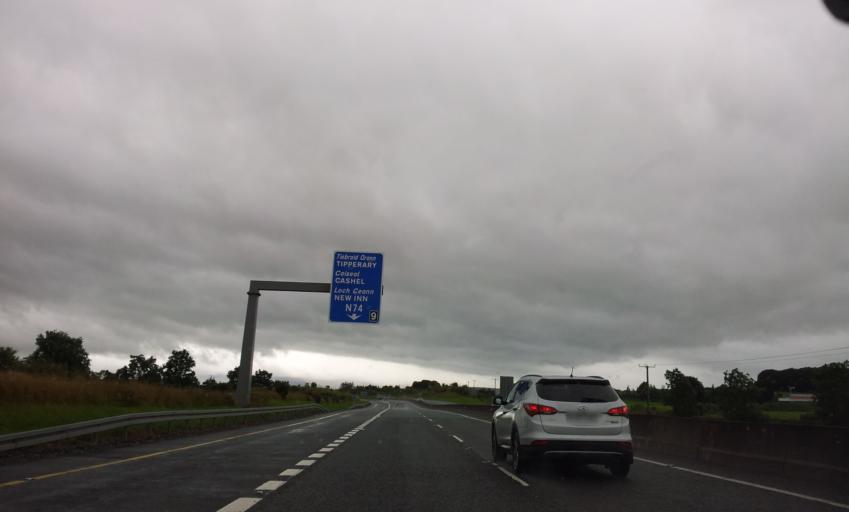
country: IE
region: Munster
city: Cashel
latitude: 52.5035
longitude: -7.8798
